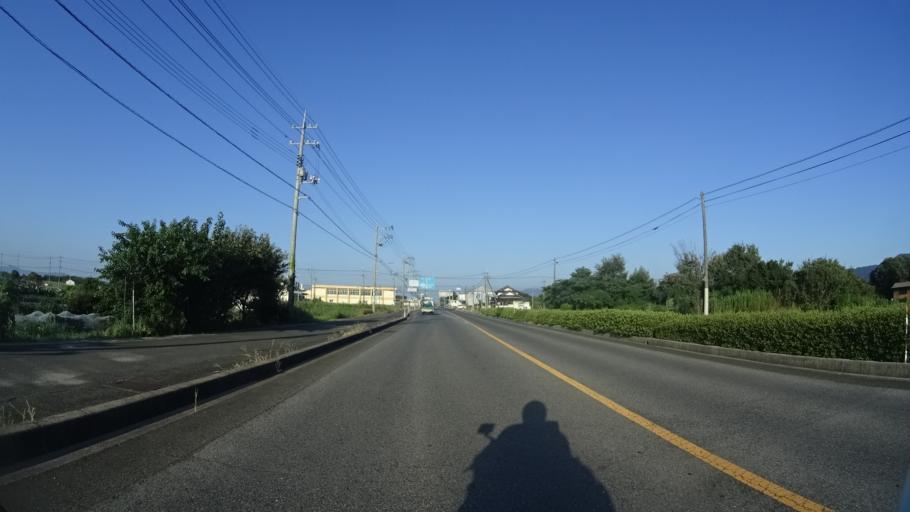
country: JP
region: Shimane
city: Sakaiminato
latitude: 35.5218
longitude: 133.2338
